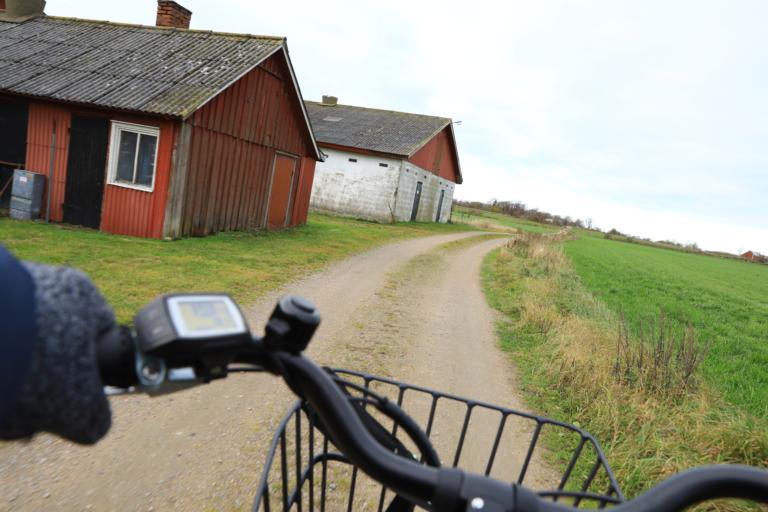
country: SE
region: Halland
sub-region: Varbergs Kommun
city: Traslovslage
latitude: 57.0587
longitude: 12.3287
